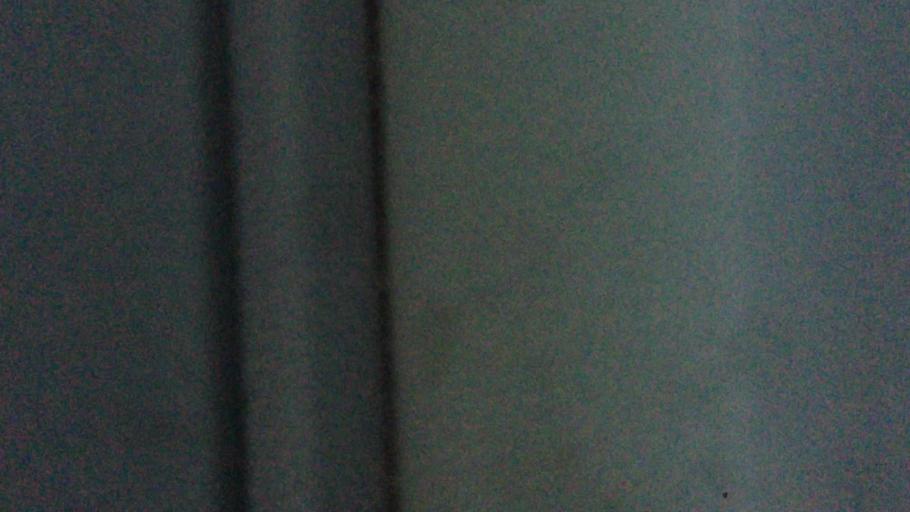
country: US
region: New York
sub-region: Dutchess County
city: Rhinebeck
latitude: 41.9584
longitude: -73.9208
